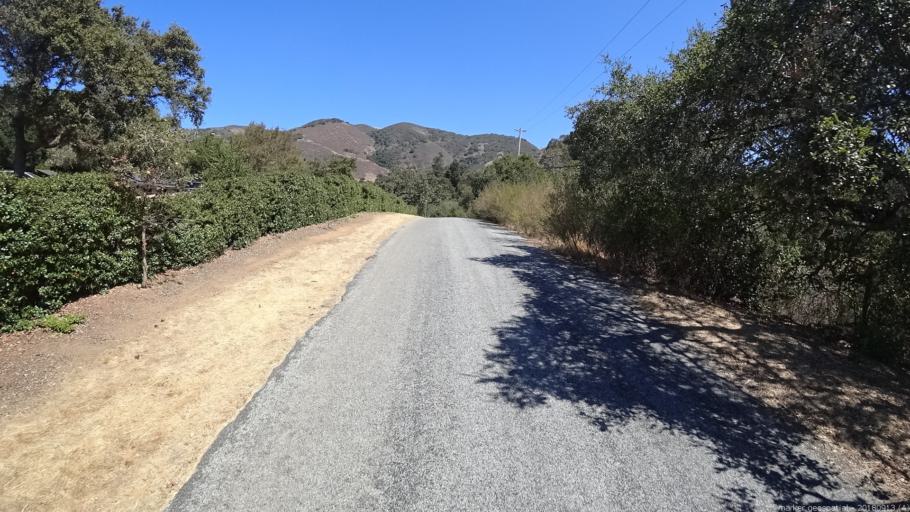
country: US
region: California
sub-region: Monterey County
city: Carmel Valley Village
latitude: 36.5039
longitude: -121.7551
